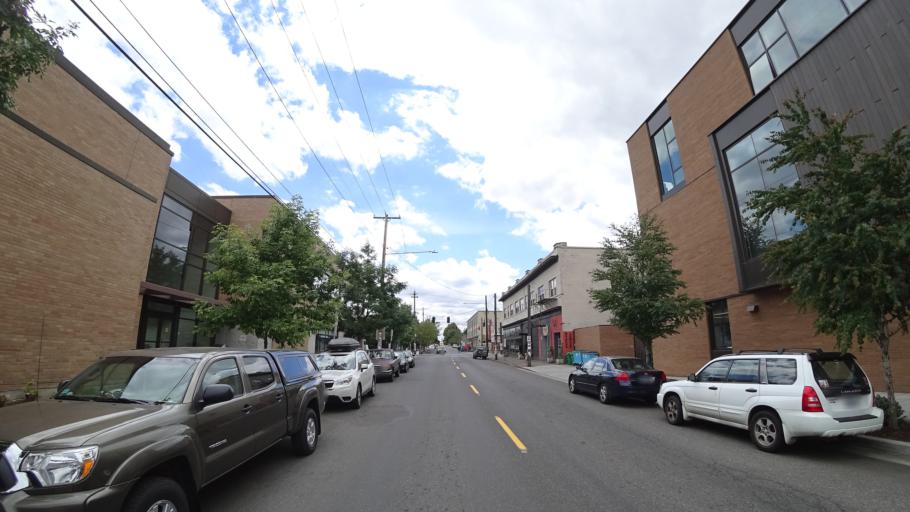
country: US
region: Oregon
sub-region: Multnomah County
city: Portland
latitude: 45.5633
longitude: -122.6750
